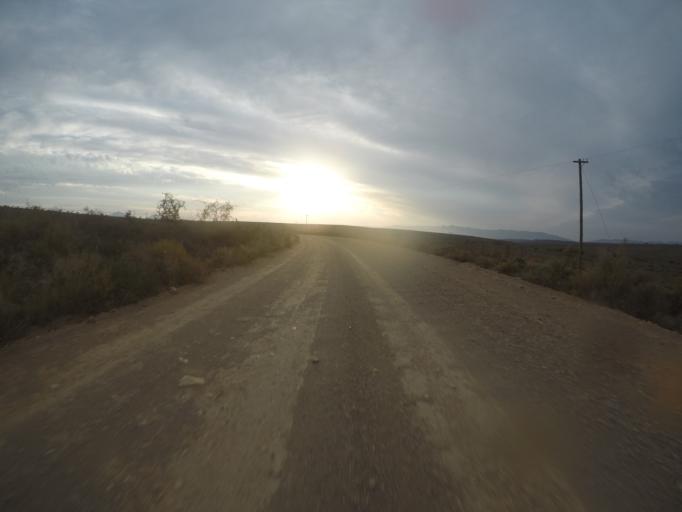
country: ZA
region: Eastern Cape
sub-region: Cacadu District Municipality
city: Willowmore
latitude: -33.5765
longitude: 23.1729
